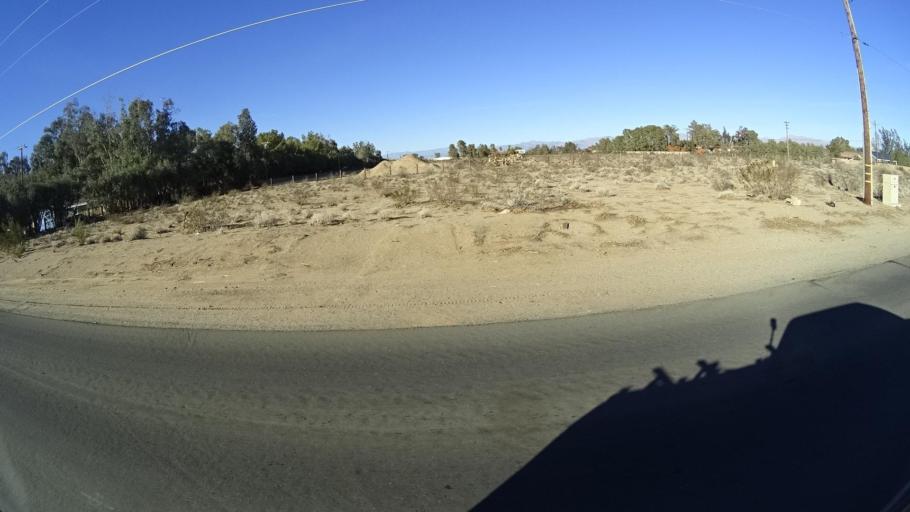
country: US
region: California
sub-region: Kern County
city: Ridgecrest
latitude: 35.6372
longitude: -117.7071
